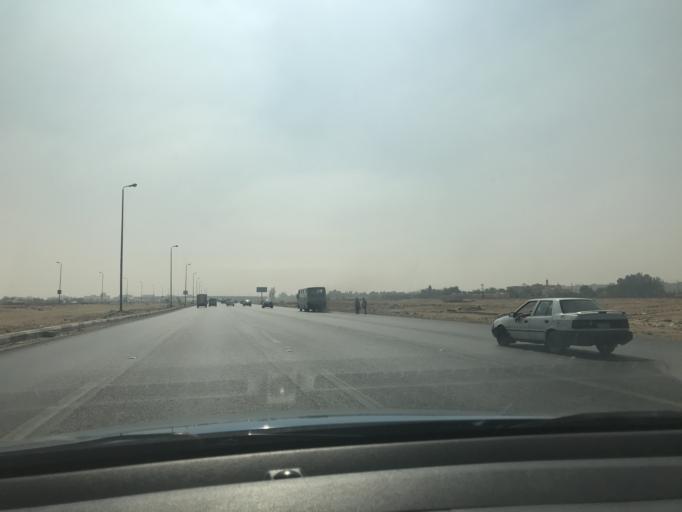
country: EG
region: Muhafazat al Qalyubiyah
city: Al Khankah
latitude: 30.1749
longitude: 31.5610
